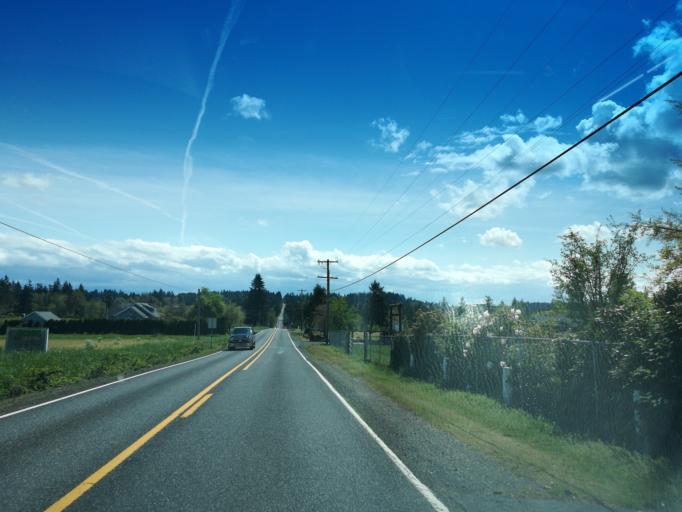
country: US
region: Oregon
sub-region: Clackamas County
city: Damascus
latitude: 45.4481
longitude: -122.4346
